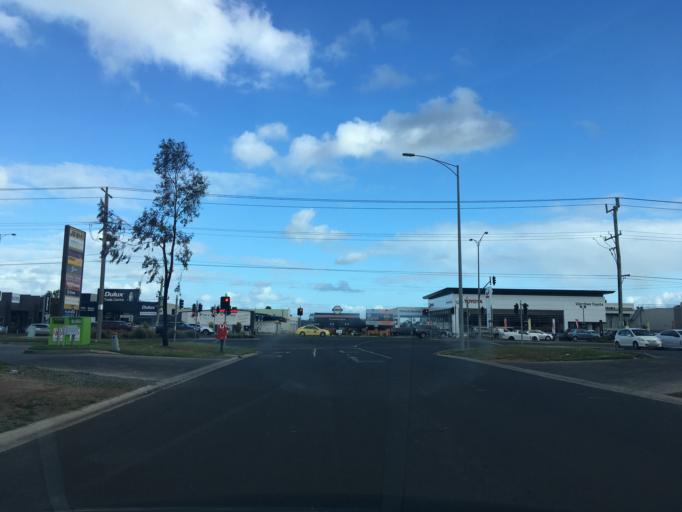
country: AU
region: Victoria
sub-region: Wyndham
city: Hoppers Crossing
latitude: -37.8744
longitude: 144.7178
